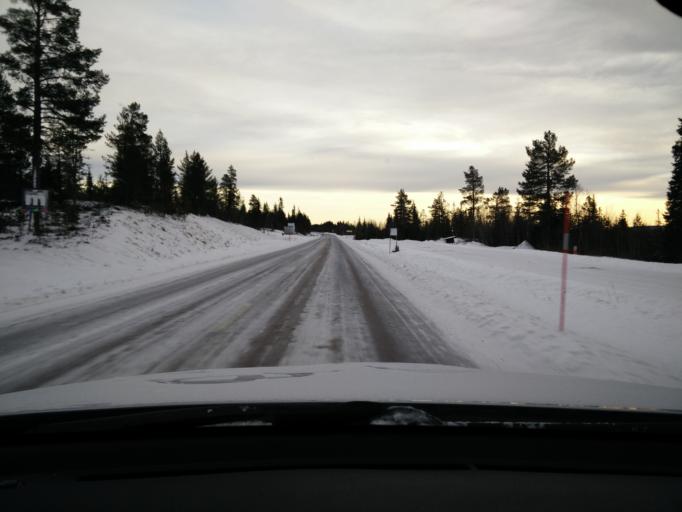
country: SE
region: Jaemtland
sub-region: Bergs Kommun
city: Hoverberg
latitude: 62.4780
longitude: 14.1340
